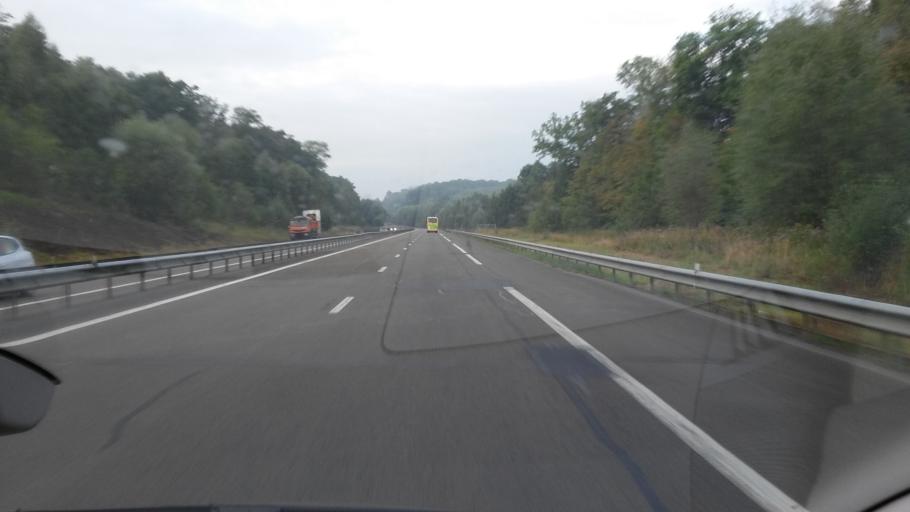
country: FR
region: Champagne-Ardenne
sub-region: Departement des Ardennes
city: Attigny
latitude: 49.6391
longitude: 4.5670
